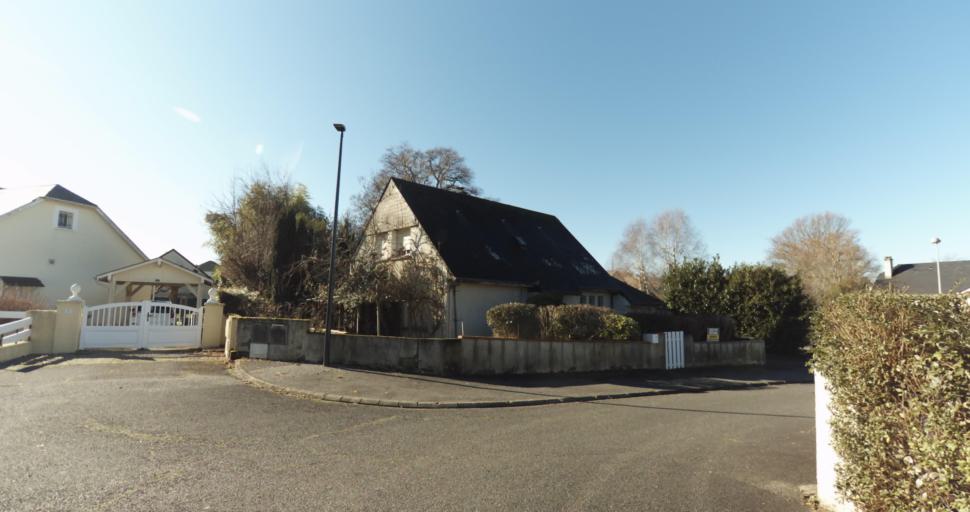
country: FR
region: Aquitaine
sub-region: Departement des Pyrenees-Atlantiques
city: Morlaas
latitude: 43.3482
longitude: -0.2637
